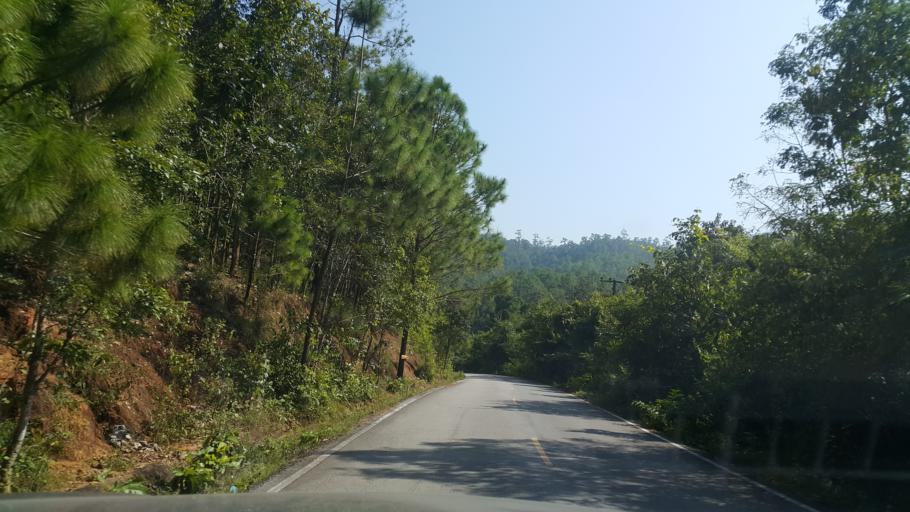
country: TH
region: Chiang Mai
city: Samoeng
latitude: 18.8675
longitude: 98.6274
